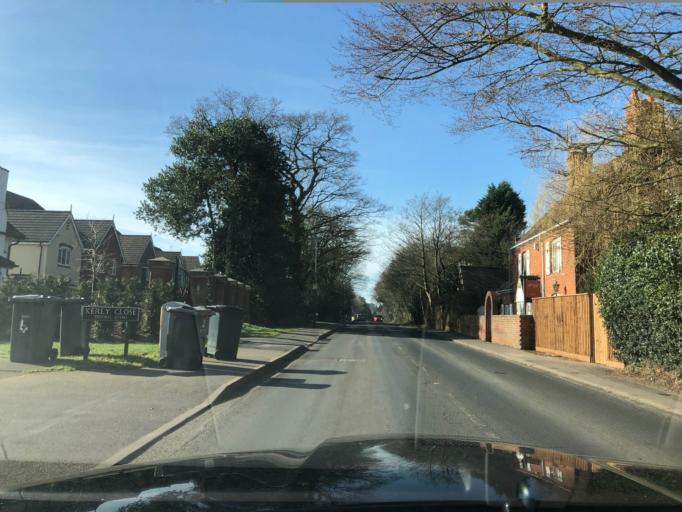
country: GB
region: England
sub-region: Solihull
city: Balsall Common
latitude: 52.3843
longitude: -1.6389
